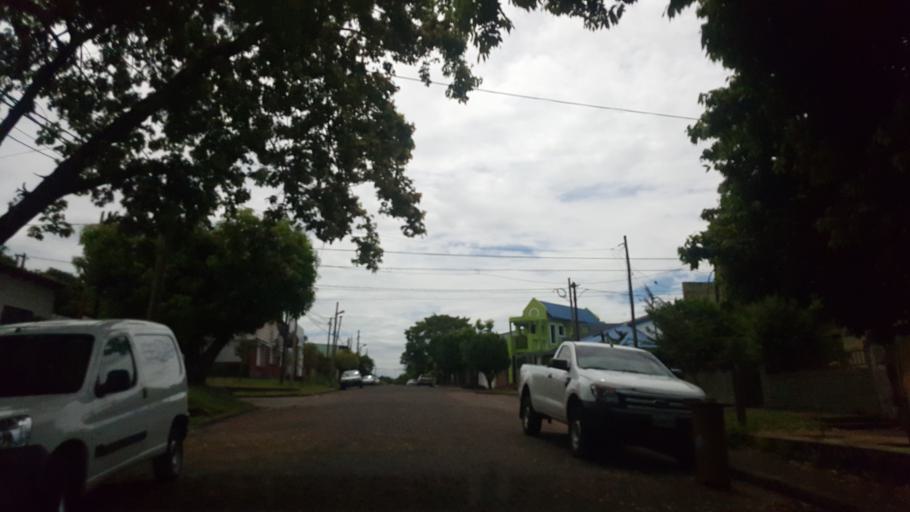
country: AR
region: Misiones
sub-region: Departamento de Capital
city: Posadas
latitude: -27.3898
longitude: -55.9027
